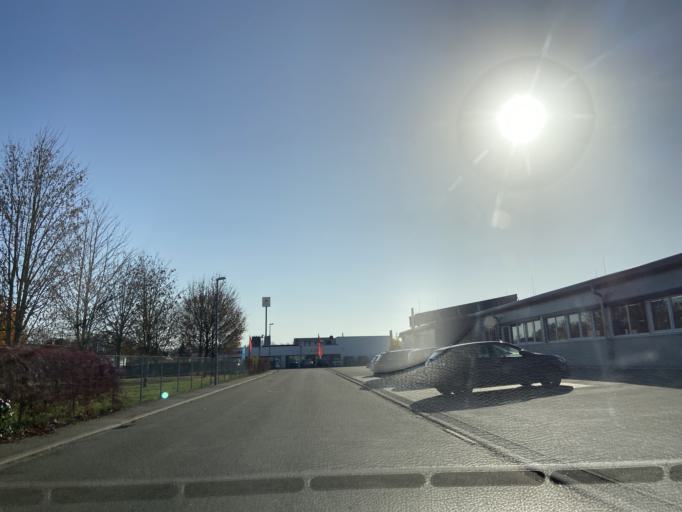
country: DE
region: Baden-Wuerttemberg
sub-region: Tuebingen Region
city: Mengen
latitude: 48.0582
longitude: 9.3429
